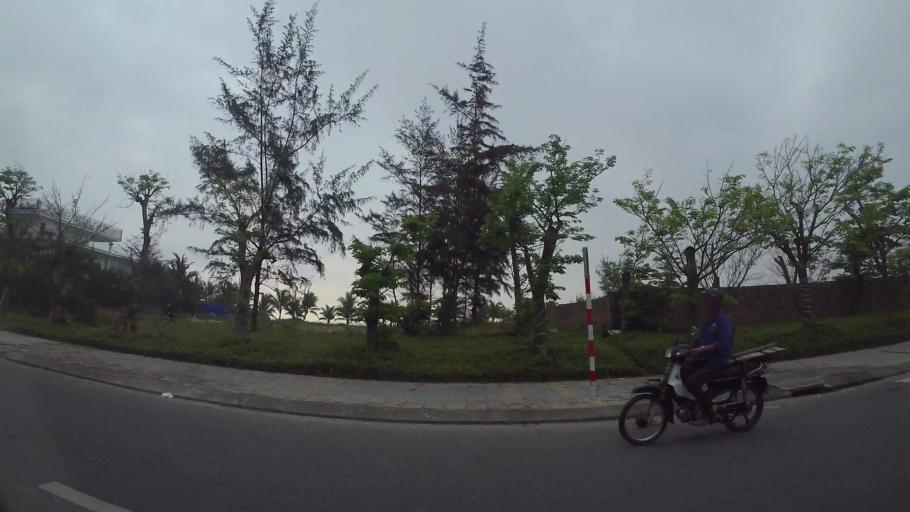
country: VN
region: Da Nang
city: Son Tra
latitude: 16.0796
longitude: 108.2465
